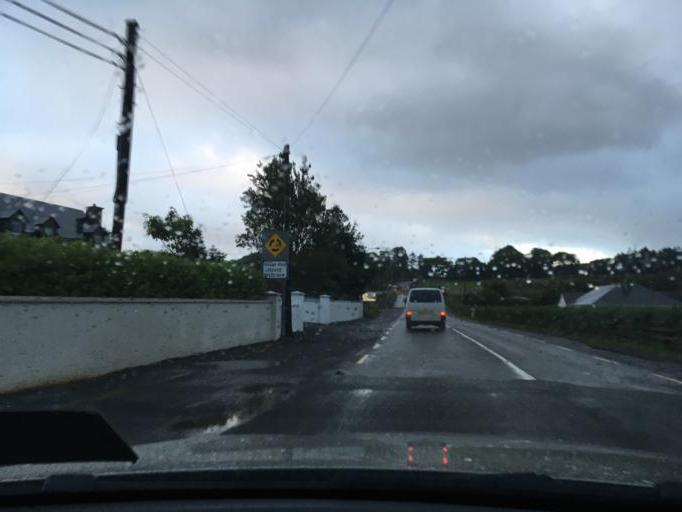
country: IE
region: Ulster
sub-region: County Donegal
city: Killybegs
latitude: 54.6347
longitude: -8.4639
